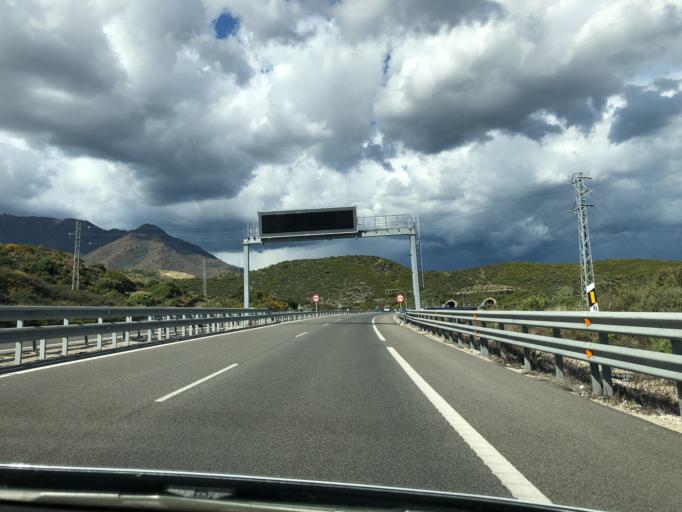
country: ES
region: Andalusia
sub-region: Provincia de Malaga
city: Manilva
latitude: 36.4201
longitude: -5.2188
